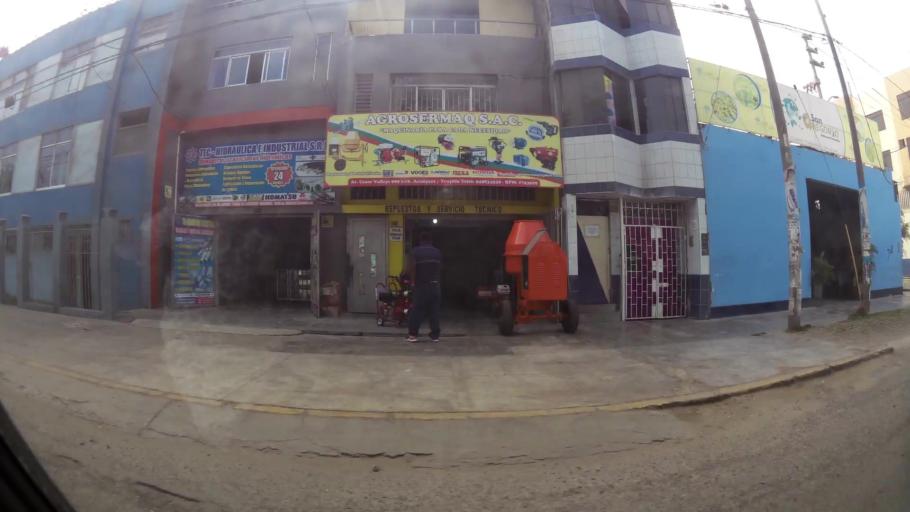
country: PE
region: La Libertad
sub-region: Provincia de Trujillo
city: Trujillo
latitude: -8.1050
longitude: -79.0131
